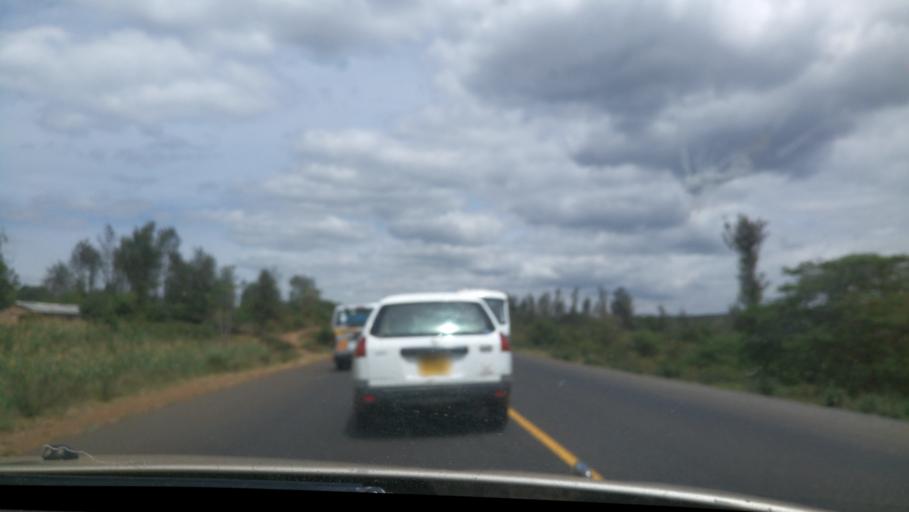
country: KE
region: Murang'a District
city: Maragua
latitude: -0.8368
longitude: 37.2312
